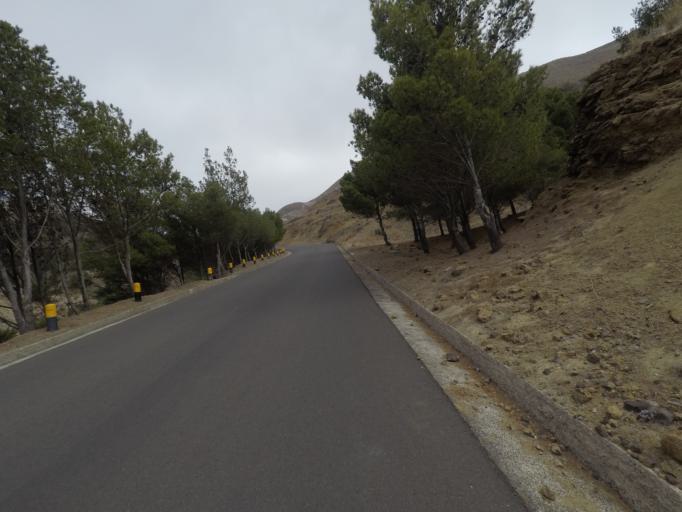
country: PT
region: Madeira
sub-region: Porto Santo
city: Camacha
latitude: 33.0912
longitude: -16.3108
